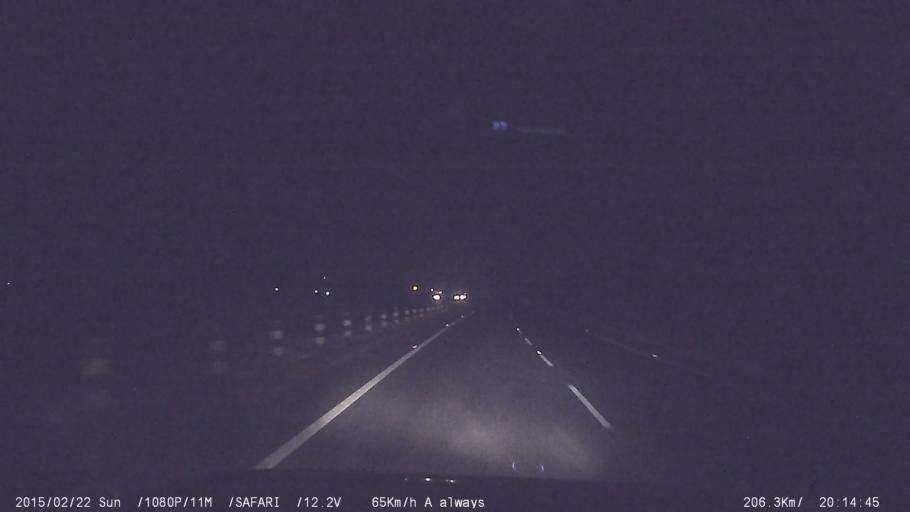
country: IN
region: Tamil Nadu
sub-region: Dindigul
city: Nilakottai
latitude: 10.2565
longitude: 77.8347
